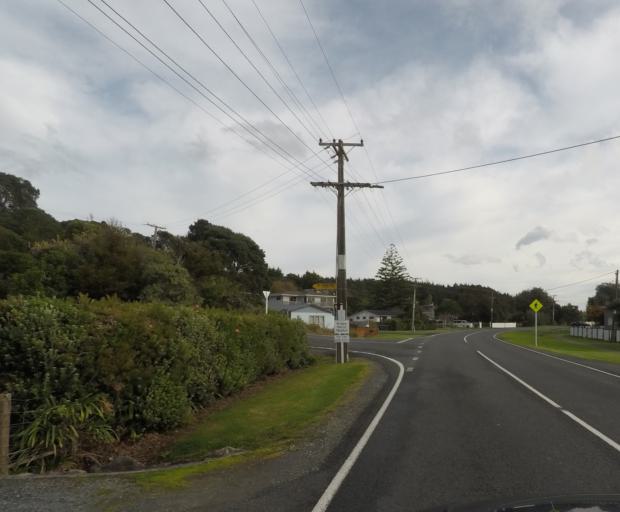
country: NZ
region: Northland
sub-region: Whangarei
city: Ruakaka
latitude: -36.0287
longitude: 174.5037
